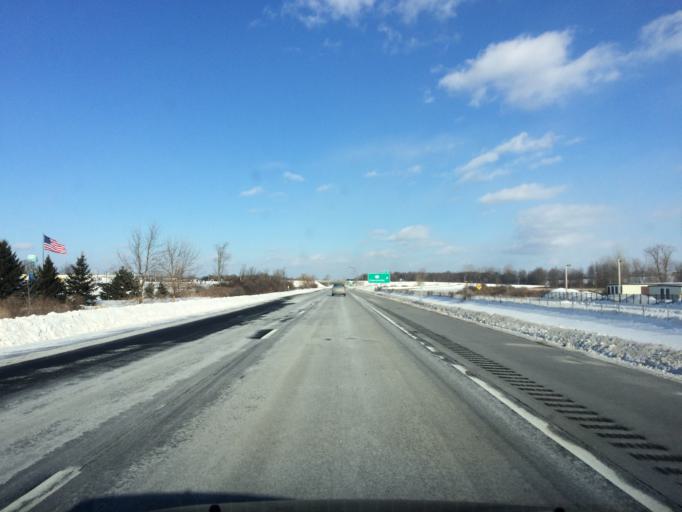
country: US
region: New York
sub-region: Monroe County
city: Churchville
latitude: 43.0910
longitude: -77.8920
